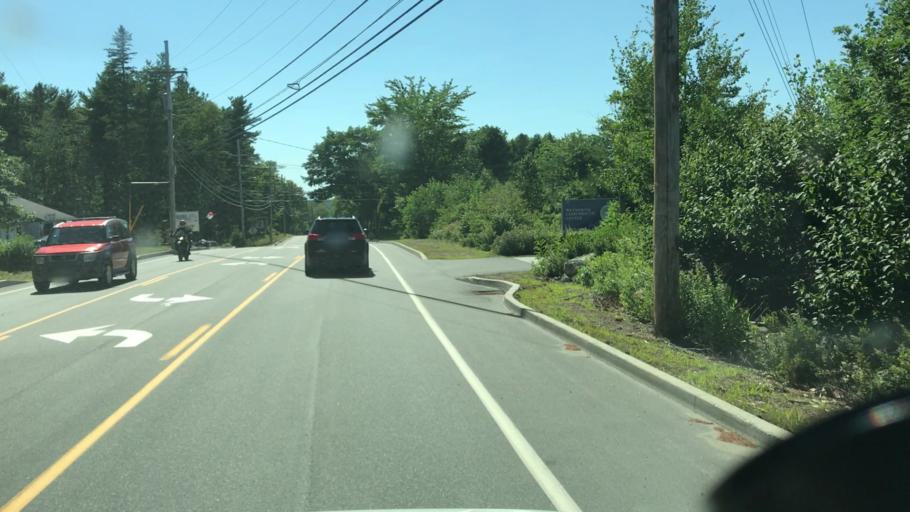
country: US
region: Maine
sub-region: Hancock County
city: Ellsworth
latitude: 44.5192
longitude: -68.3974
